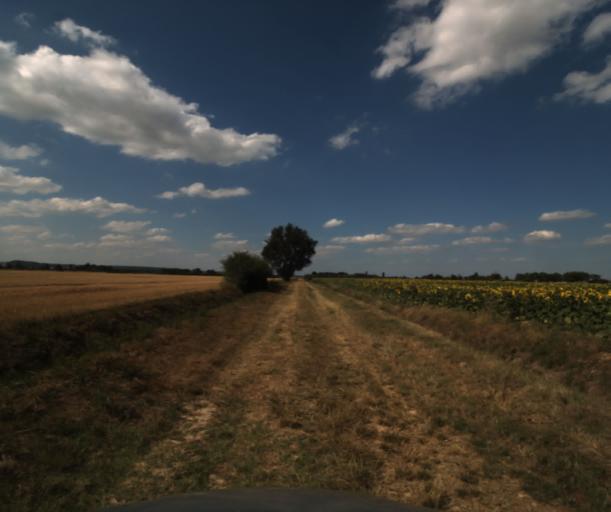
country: FR
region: Midi-Pyrenees
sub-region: Departement de la Haute-Garonne
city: Saint-Lys
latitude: 43.5231
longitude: 1.1778
